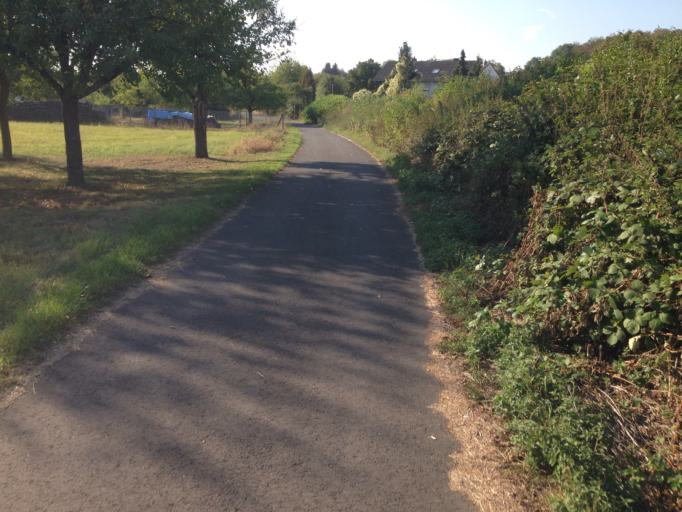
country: DE
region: Hesse
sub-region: Regierungsbezirk Giessen
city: Giessen
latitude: 50.5445
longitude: 8.7352
